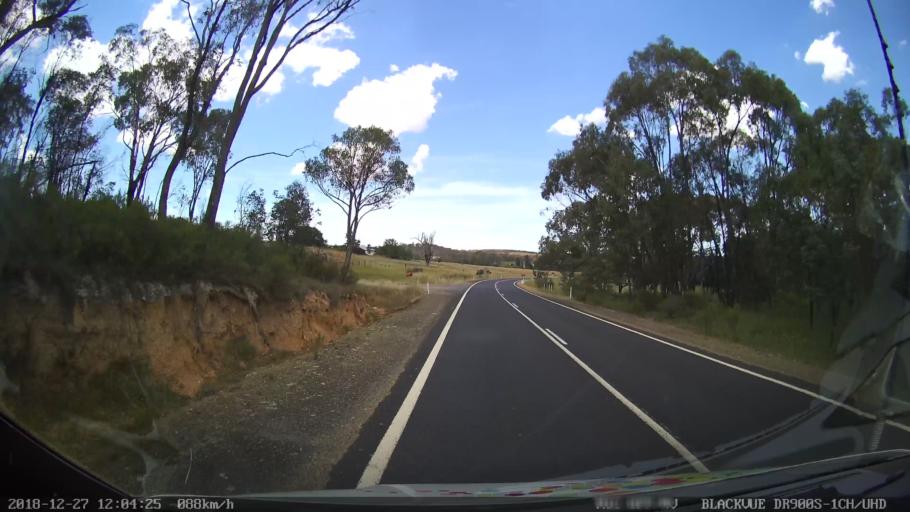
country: AU
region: New South Wales
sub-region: Blayney
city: Blayney
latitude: -33.7967
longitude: 149.3507
